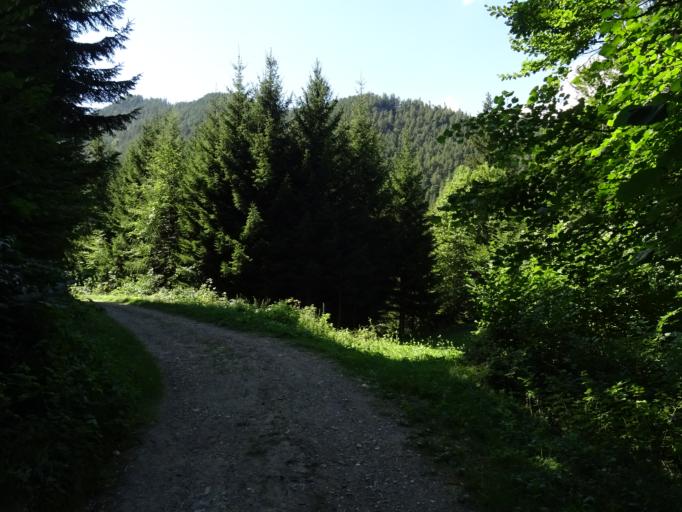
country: AT
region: Lower Austria
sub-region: Politischer Bezirk Neunkirchen
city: Semmering
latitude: 47.6477
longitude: 15.8150
